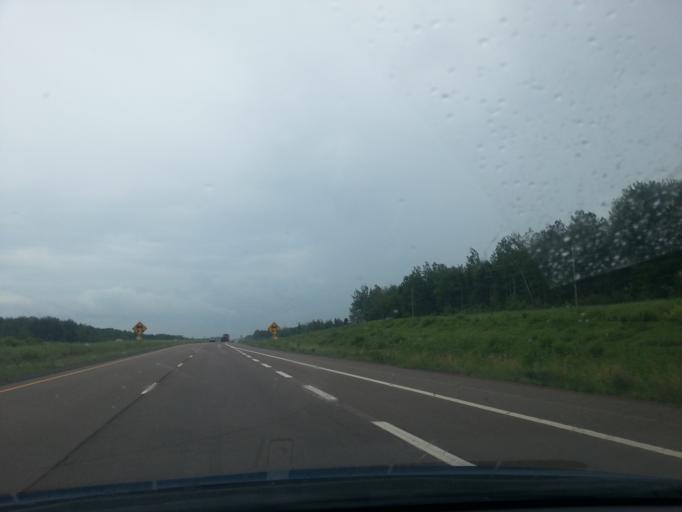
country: CA
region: New Brunswick
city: Moncton
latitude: 46.1288
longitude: -64.8238
